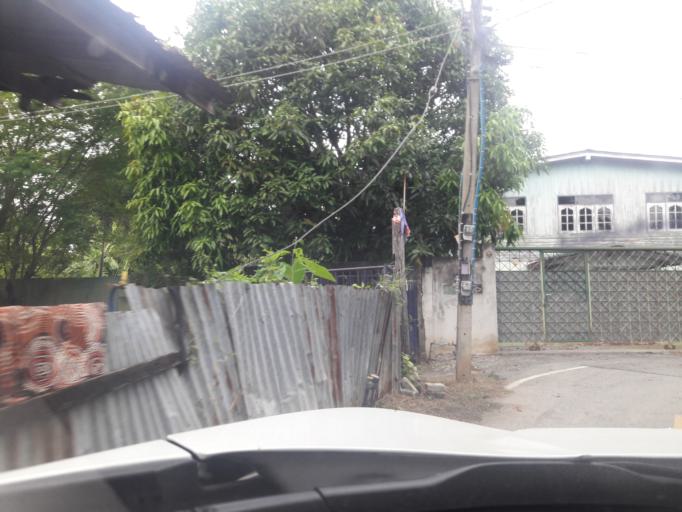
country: TH
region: Lop Buri
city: Ban Mi
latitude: 15.0458
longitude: 100.5471
